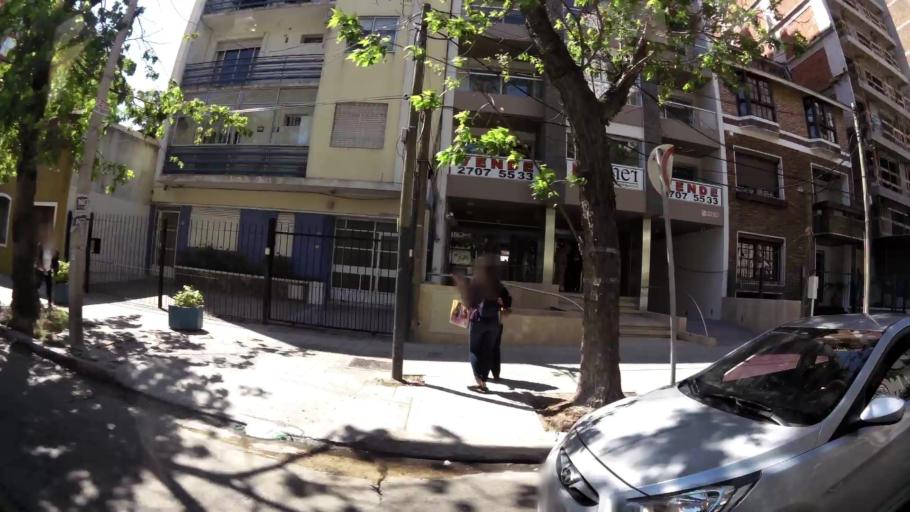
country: UY
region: Montevideo
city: Montevideo
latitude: -34.9070
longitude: -56.1435
